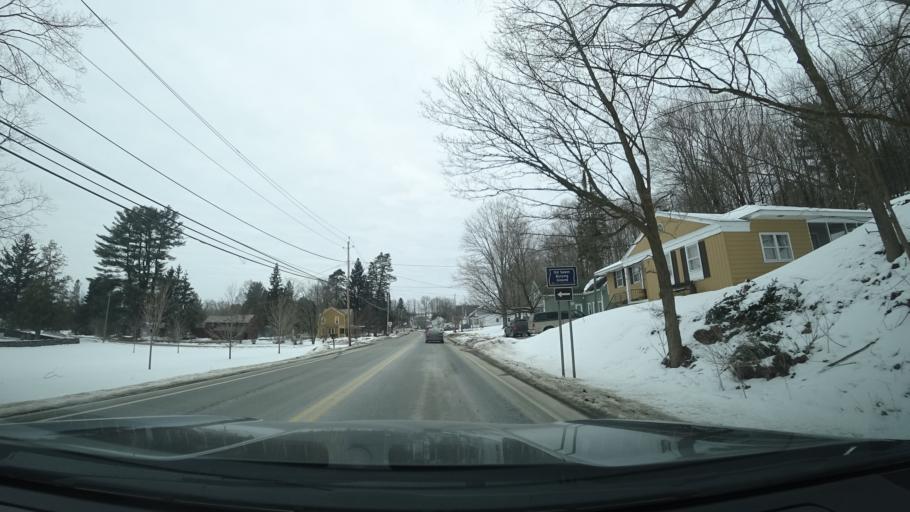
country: US
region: New York
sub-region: Washington County
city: Cambridge
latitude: 43.1662
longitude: -73.3284
